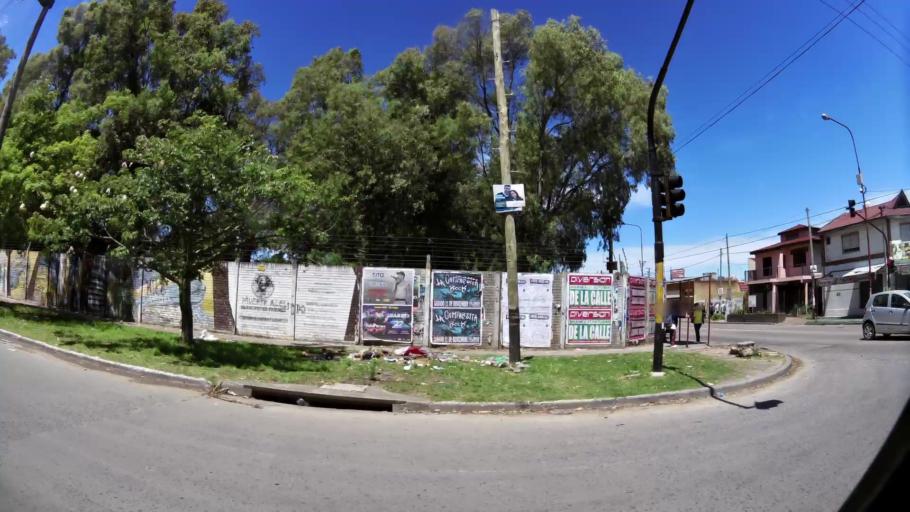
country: AR
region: Buenos Aires
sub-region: Partido de Quilmes
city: Quilmes
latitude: -34.7377
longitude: -58.2988
